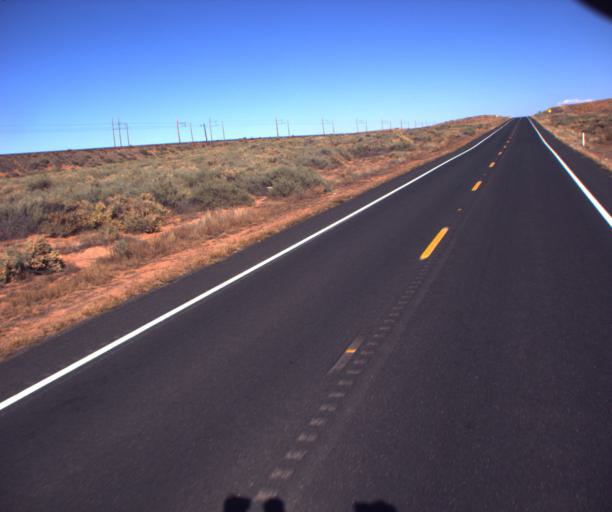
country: US
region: Arizona
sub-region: Coconino County
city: Kaibito
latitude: 36.3934
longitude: -110.8748
